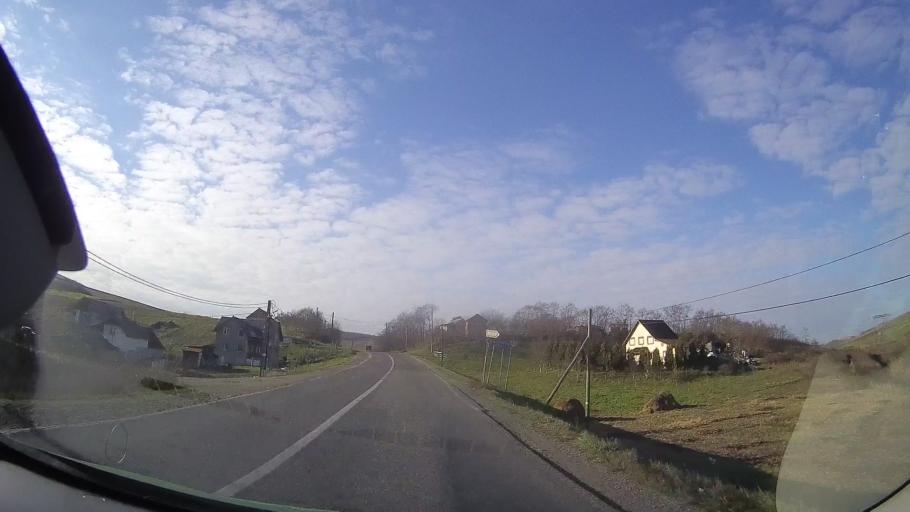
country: RO
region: Cluj
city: Caianu Mic
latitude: 46.8124
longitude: 23.8689
